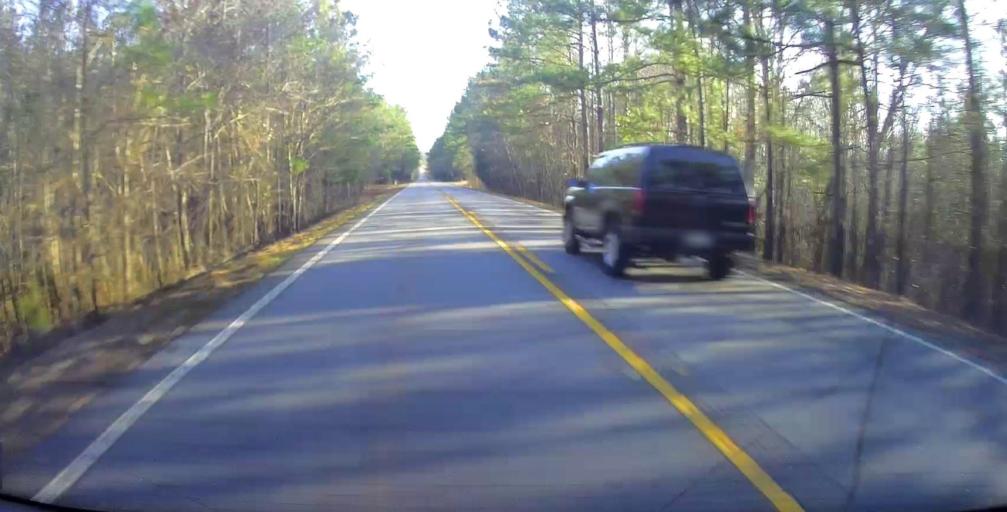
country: US
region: Alabama
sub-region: Chambers County
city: Valley
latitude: 32.8052
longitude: -85.1031
